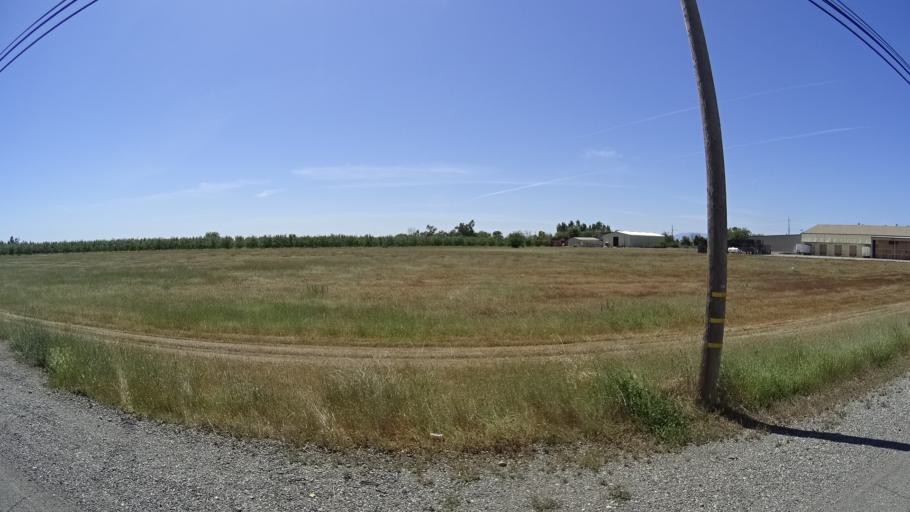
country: US
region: California
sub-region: Glenn County
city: Orland
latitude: 39.7388
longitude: -122.1749
